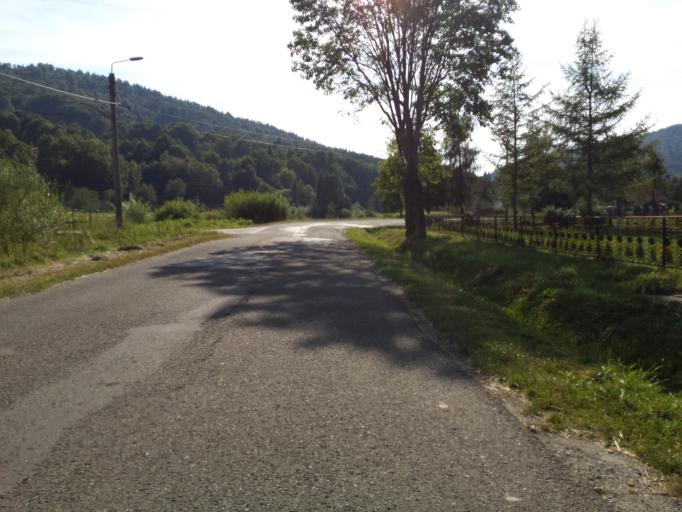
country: PL
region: Subcarpathian Voivodeship
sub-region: Powiat leski
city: Olszanica
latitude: 49.5085
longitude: 22.4719
